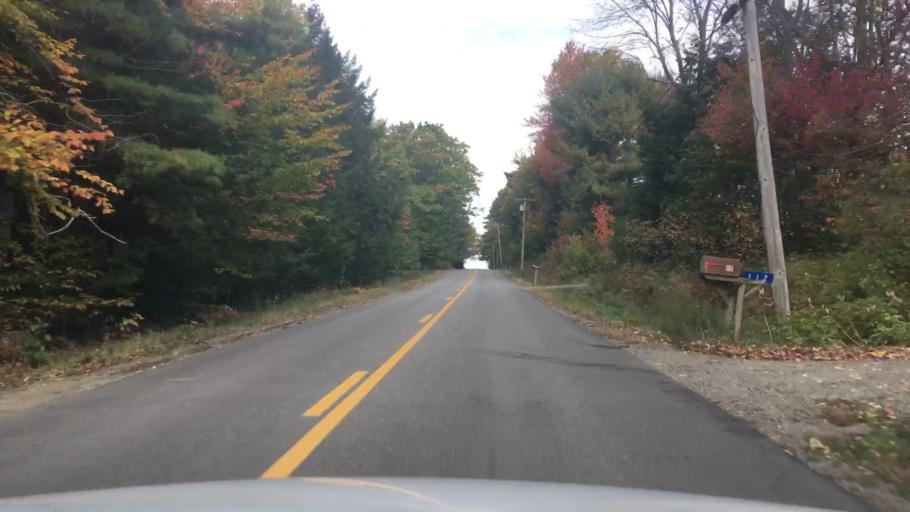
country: US
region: Maine
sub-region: Waldo County
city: Searsmont
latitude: 44.3897
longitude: -69.1336
